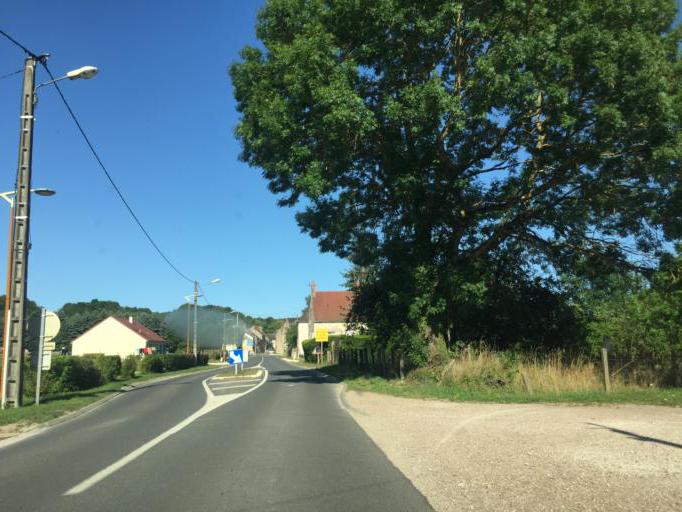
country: FR
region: Bourgogne
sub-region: Departement de l'Yonne
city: Fontenailles
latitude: 47.4804
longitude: 3.4176
